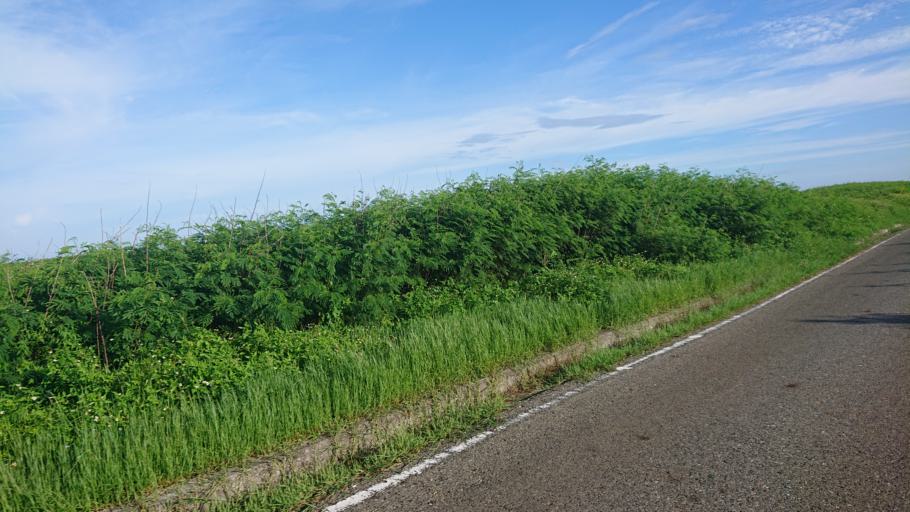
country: TW
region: Taiwan
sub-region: Penghu
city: Ma-kung
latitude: 23.5992
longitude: 119.5177
